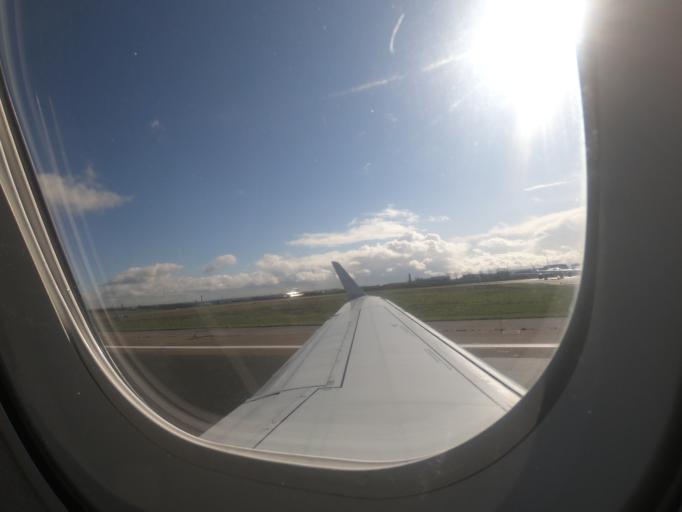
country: FR
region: Ile-de-France
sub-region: Departement du Val-d'Oise
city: Vemars
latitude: 49.0234
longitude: 2.5630
